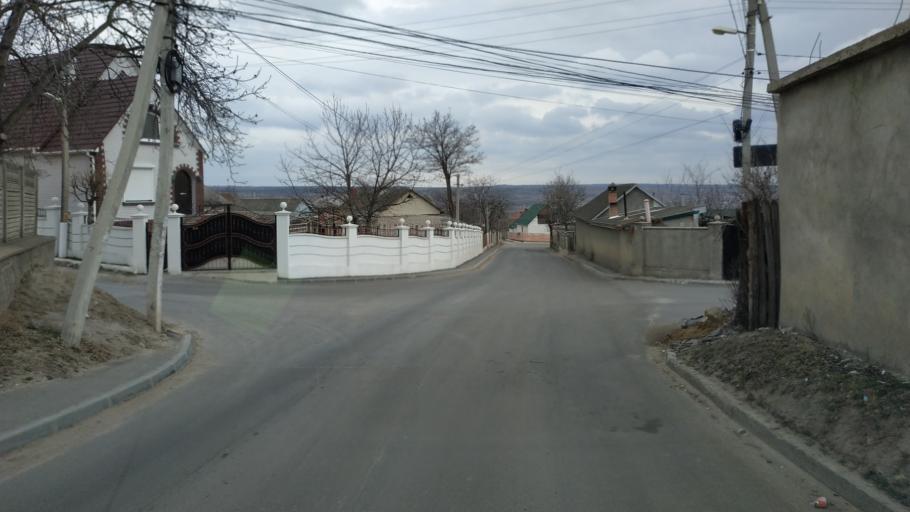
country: MD
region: Laloveni
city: Ialoveni
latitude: 46.8685
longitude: 28.7589
